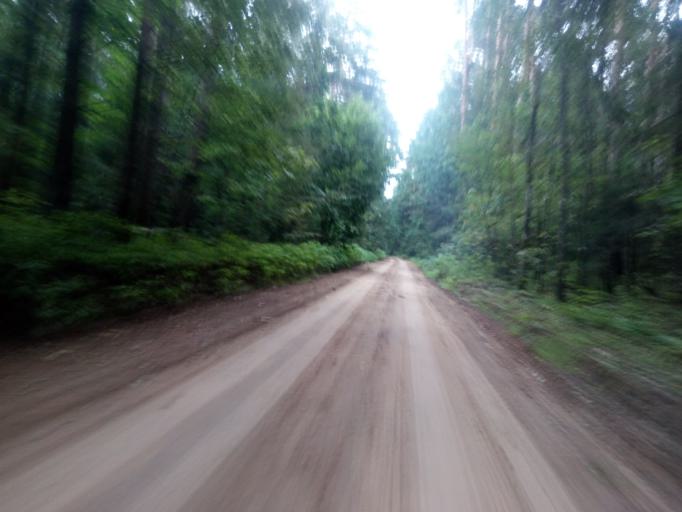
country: BY
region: Vitebsk
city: Dzisna
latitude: 55.7049
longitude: 28.3375
